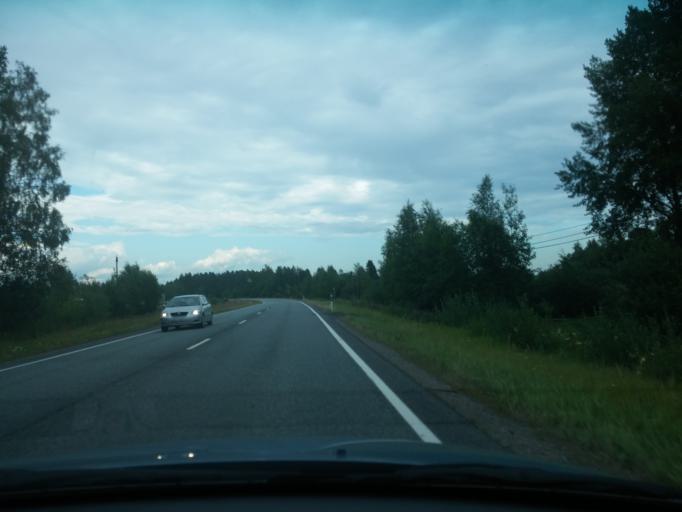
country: FI
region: Haeme
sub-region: Haemeenlinna
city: Tervakoski
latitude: 60.7402
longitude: 24.6233
